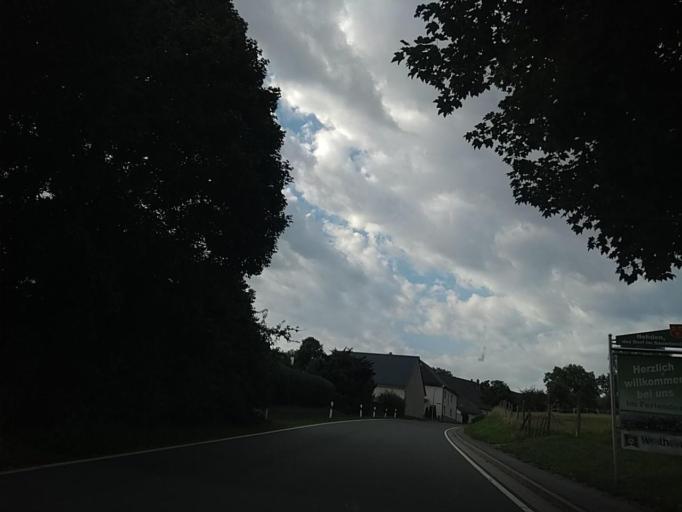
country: DE
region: North Rhine-Westphalia
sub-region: Regierungsbezirk Arnsberg
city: Brilon
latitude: 51.4392
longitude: 8.6392
